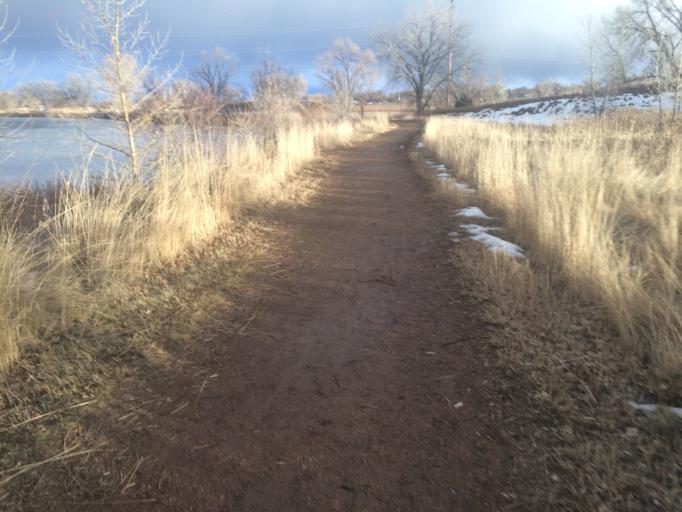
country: US
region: Colorado
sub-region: Boulder County
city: Gunbarrel
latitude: 40.0396
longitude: -105.1878
